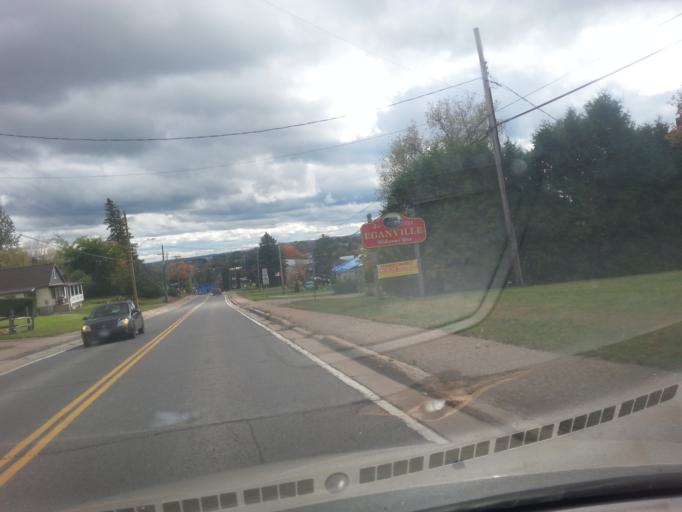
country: CA
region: Ontario
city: Pembroke
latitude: 45.5469
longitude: -77.1082
